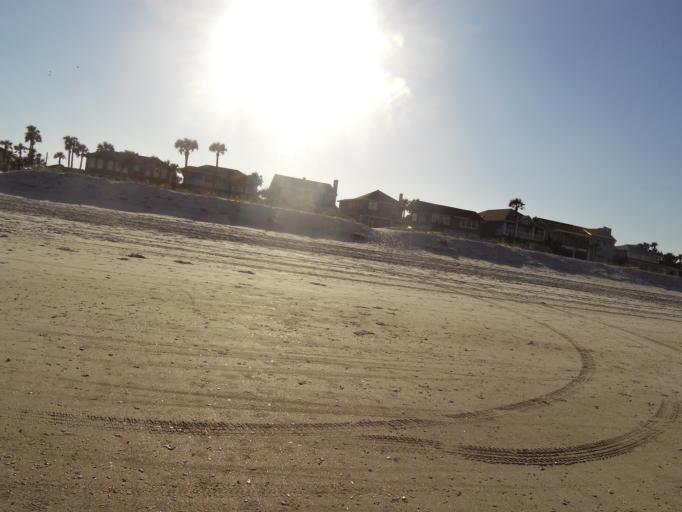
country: US
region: Florida
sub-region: Duval County
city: Atlantic Beach
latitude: 30.3431
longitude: -81.3962
